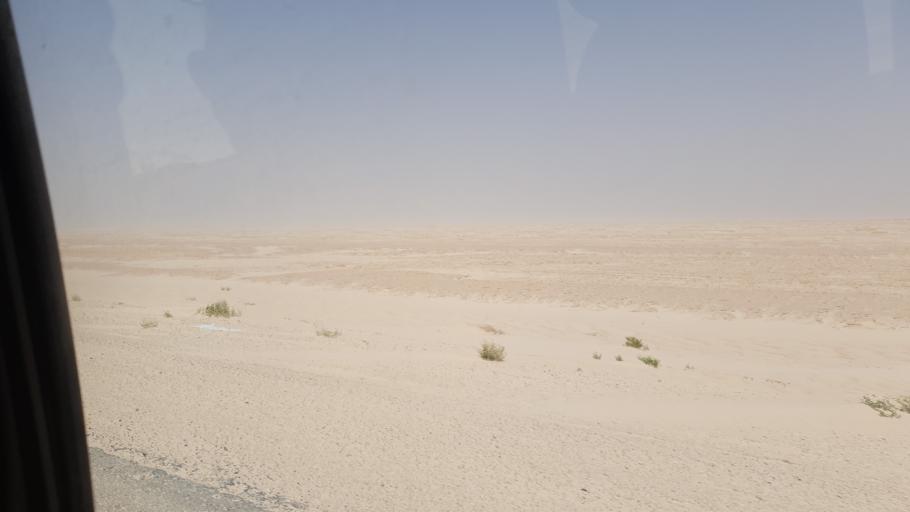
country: TN
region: Qibili
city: Kebili
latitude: 33.8692
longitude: 8.6056
